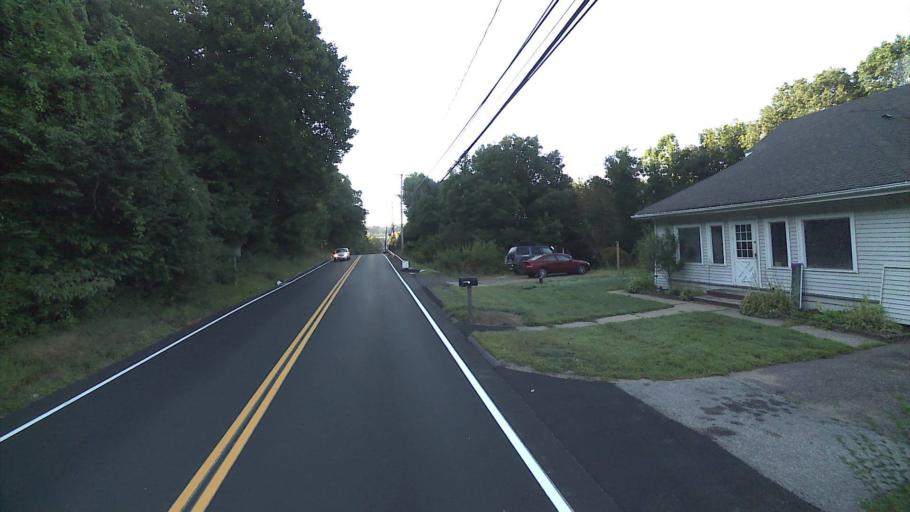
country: US
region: Connecticut
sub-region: Tolland County
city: Tolland
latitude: 41.8600
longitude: -72.3010
